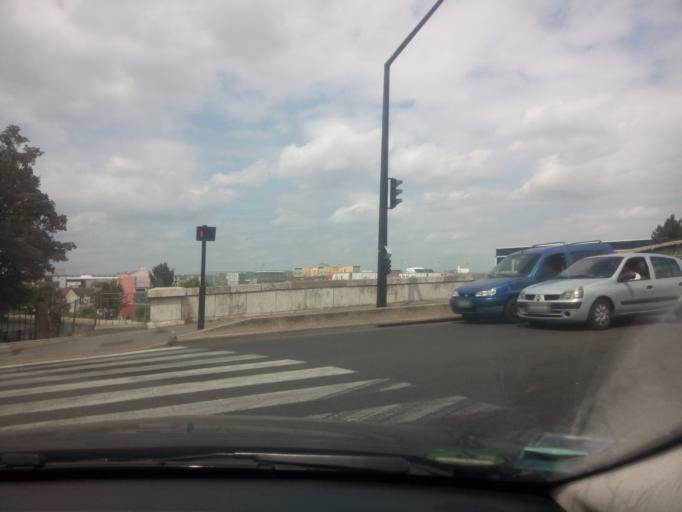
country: FR
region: Ile-de-France
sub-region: Departement de Seine-Saint-Denis
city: Aubervilliers
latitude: 48.9153
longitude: 2.3713
